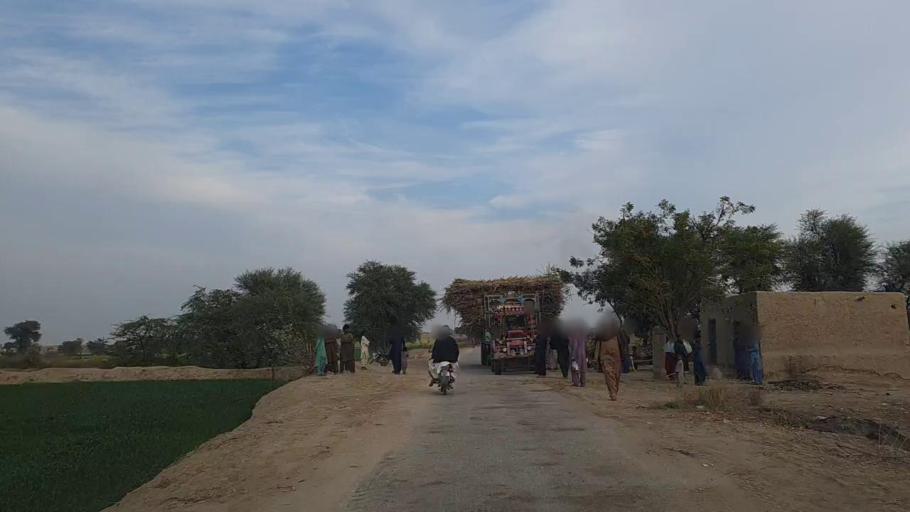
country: PK
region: Sindh
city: Daur
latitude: 26.5288
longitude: 68.4199
